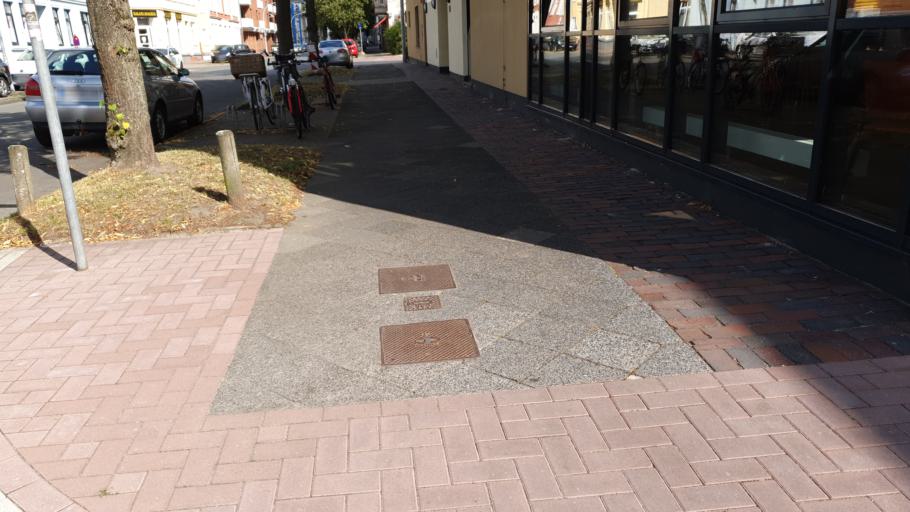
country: DE
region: Lower Saxony
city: Wilhelmshaven
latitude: 53.5180
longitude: 8.1054
